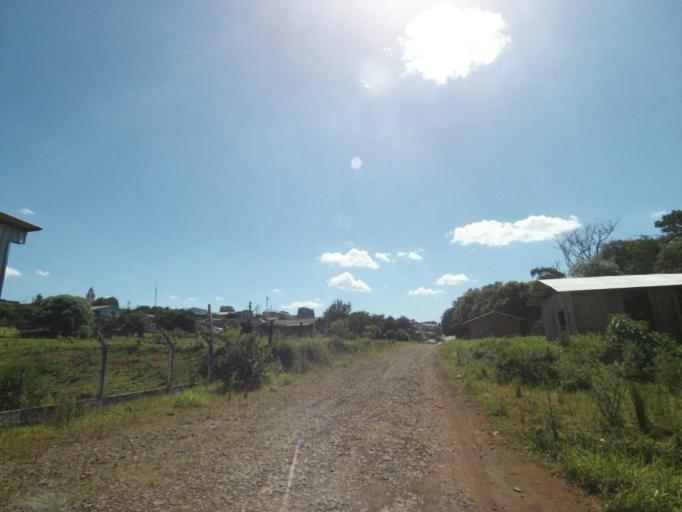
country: BR
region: Parana
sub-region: Laranjeiras Do Sul
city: Laranjeiras do Sul
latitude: -25.3791
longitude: -52.1990
